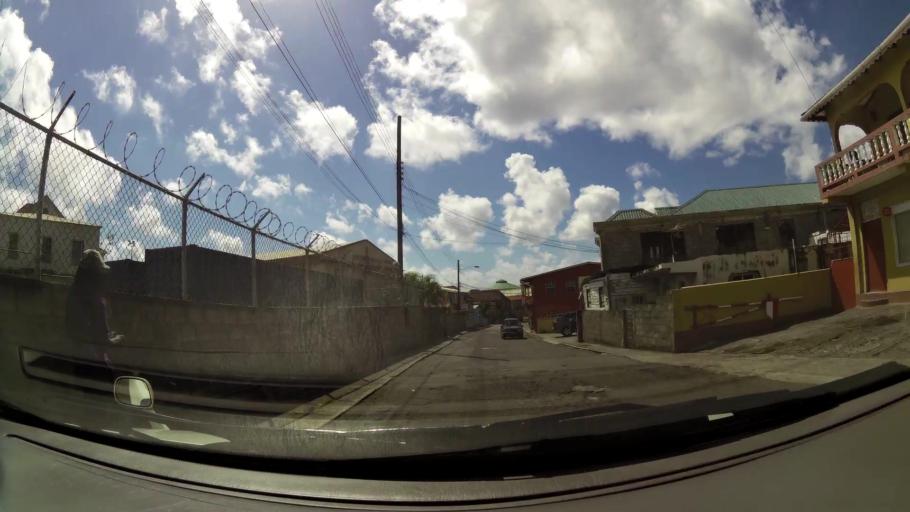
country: VC
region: Saint George
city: Kingstown Park
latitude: 13.1596
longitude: -61.2302
